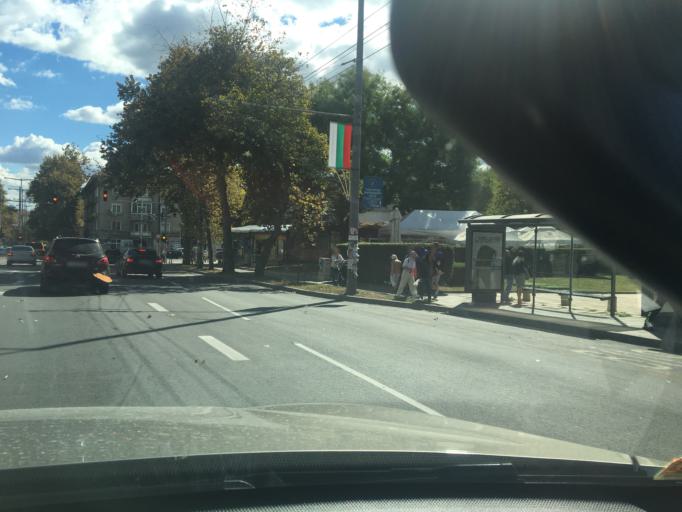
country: BG
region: Burgas
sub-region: Obshtina Burgas
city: Burgas
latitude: 42.5039
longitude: 27.4698
